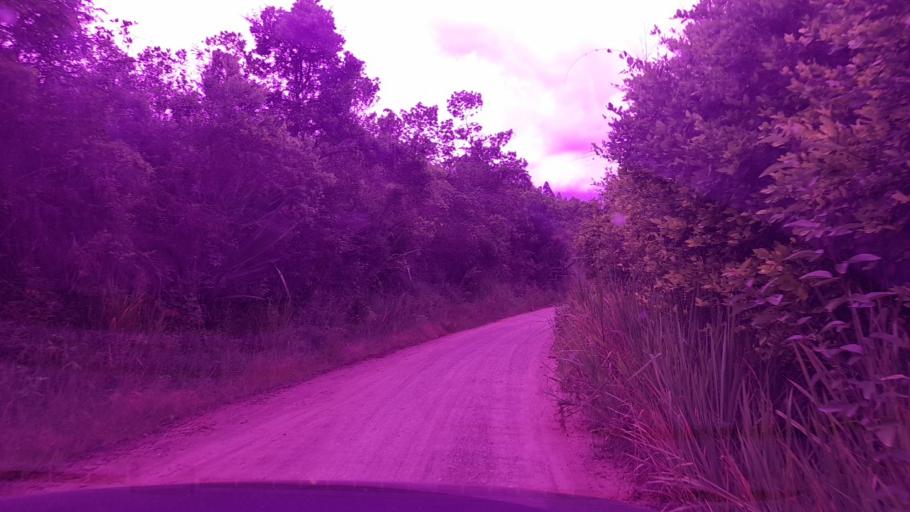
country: CO
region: Valle del Cauca
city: Andalucia
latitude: 4.1735
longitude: -76.1191
